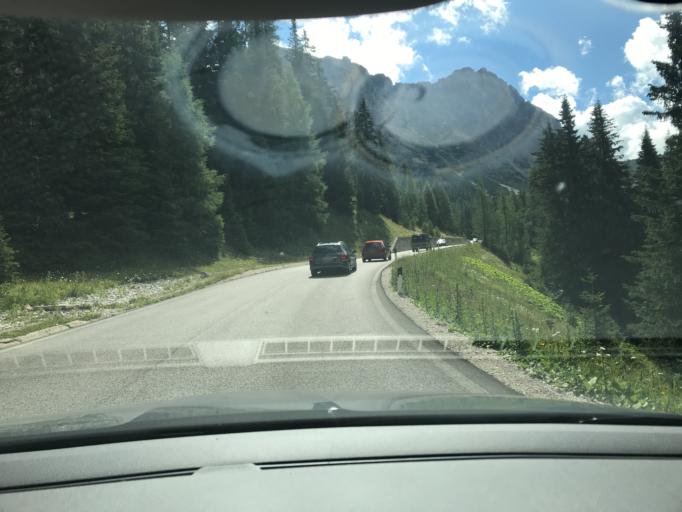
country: IT
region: Veneto
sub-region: Provincia di Belluno
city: Livinallongo del Col di Lana
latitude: 46.5428
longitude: 11.9763
